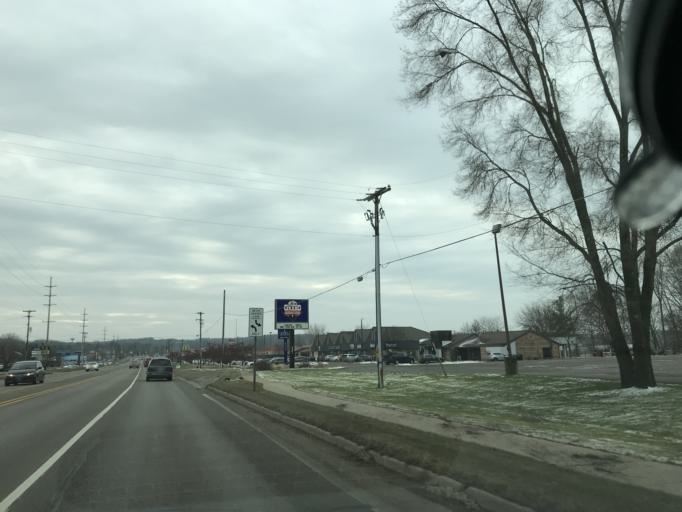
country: US
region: Michigan
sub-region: Kent County
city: Northview
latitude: 43.0626
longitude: -85.5800
